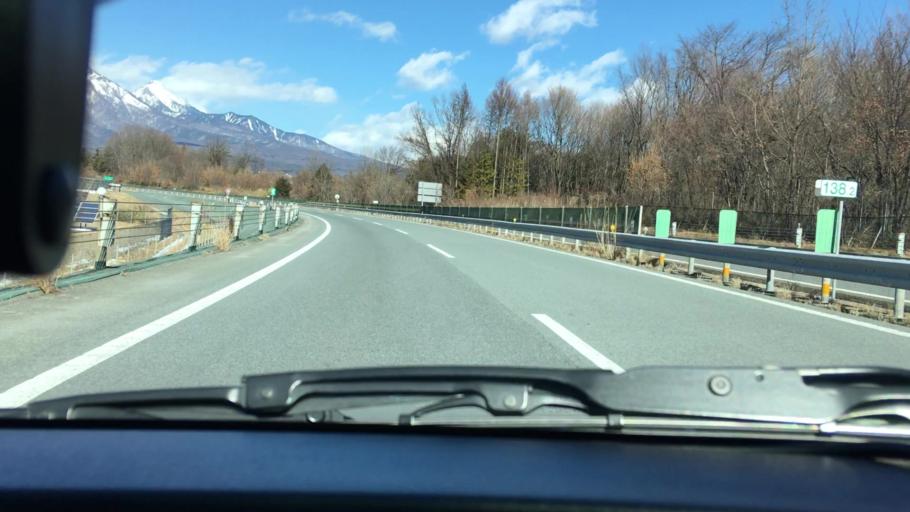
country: JP
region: Yamanashi
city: Nirasaki
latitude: 35.8211
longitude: 138.3946
